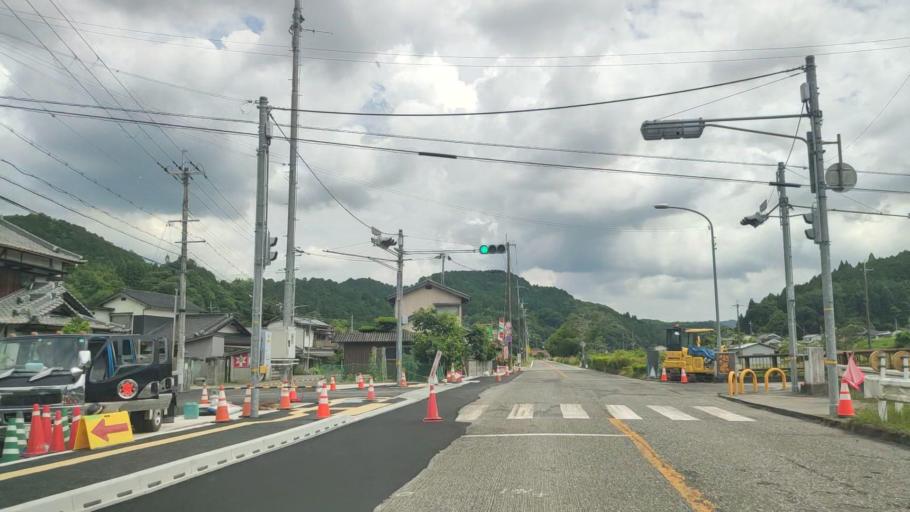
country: JP
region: Hyogo
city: Yamazakicho-nakabirose
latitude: 34.9791
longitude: 134.4426
